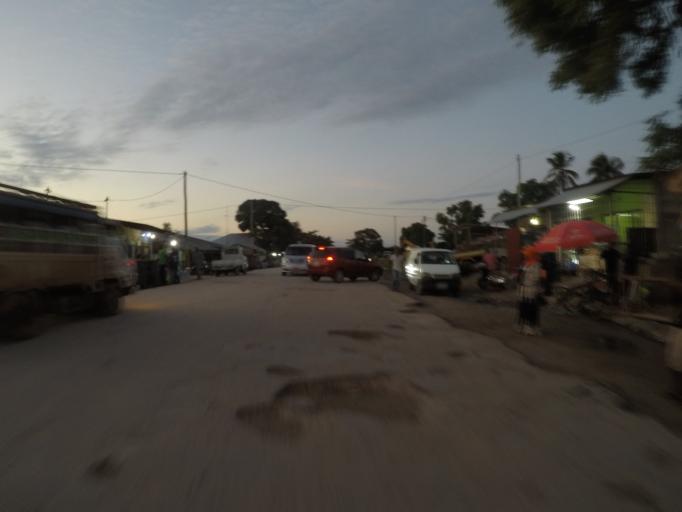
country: TZ
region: Zanzibar Central/South
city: Koani
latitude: -6.0804
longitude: 39.2221
